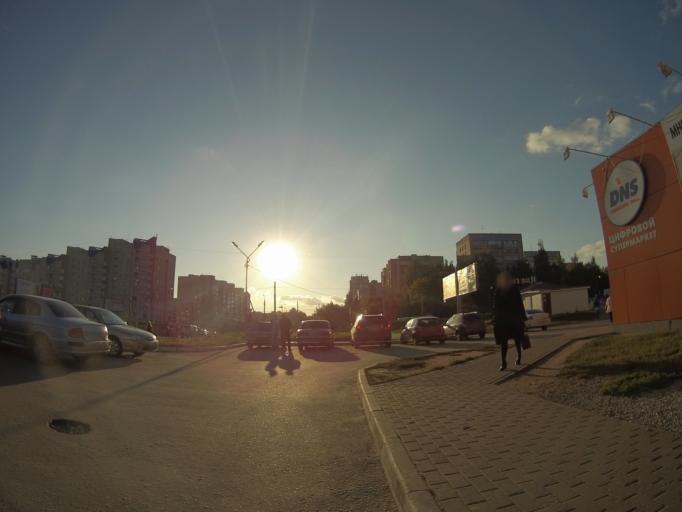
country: RU
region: Vladimir
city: Vladimir
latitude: 56.1100
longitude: 40.3461
